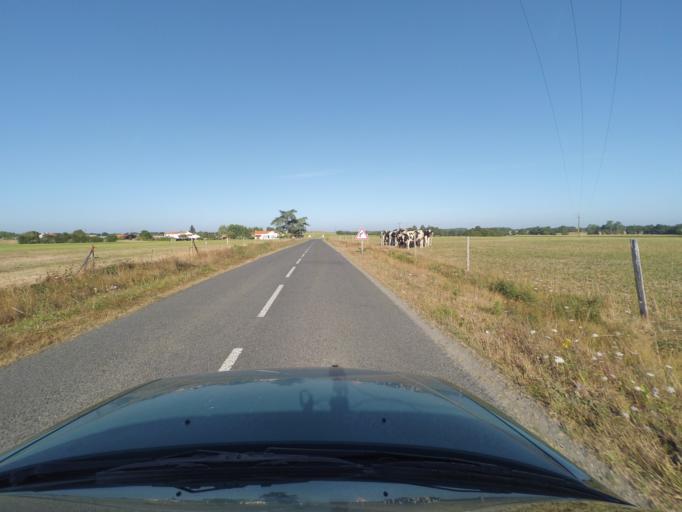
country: FR
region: Pays de la Loire
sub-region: Departement de la Loire-Atlantique
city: Le Bignon
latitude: 47.1008
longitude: -1.4998
